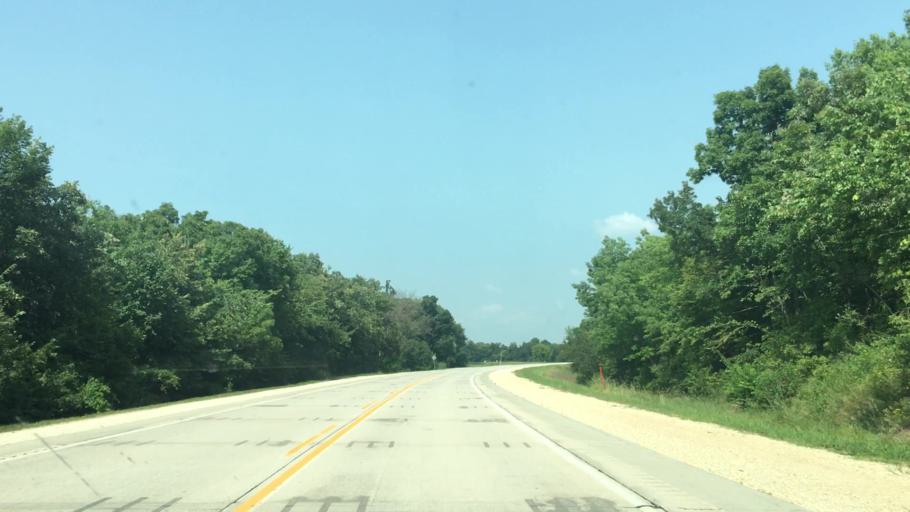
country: US
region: Iowa
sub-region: Winneshiek County
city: Decorah
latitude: 43.3406
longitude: -91.8112
